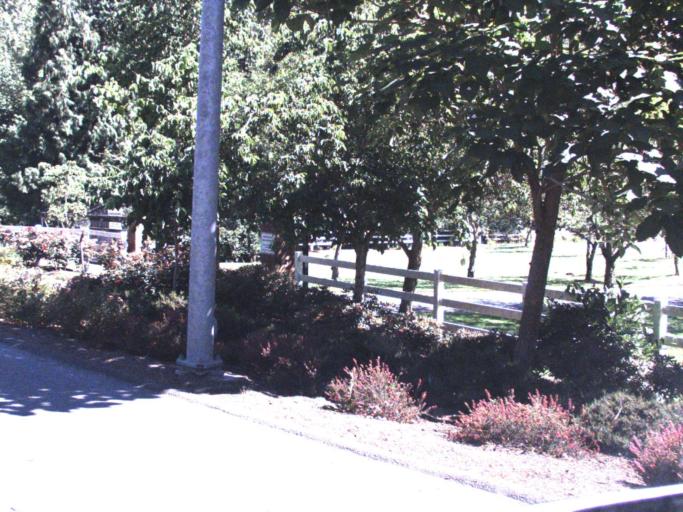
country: US
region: Washington
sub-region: King County
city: Issaquah
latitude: 47.5386
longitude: -122.0630
